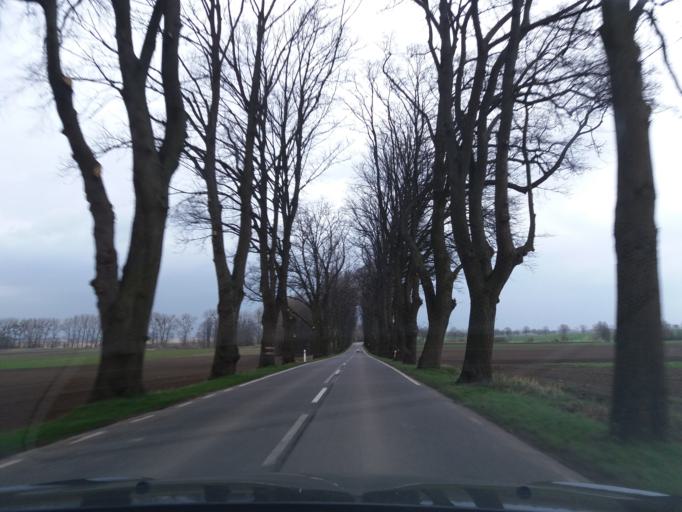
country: PL
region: West Pomeranian Voivodeship
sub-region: Powiat pyrzycki
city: Pyrzyce
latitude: 53.1387
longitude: 14.9746
